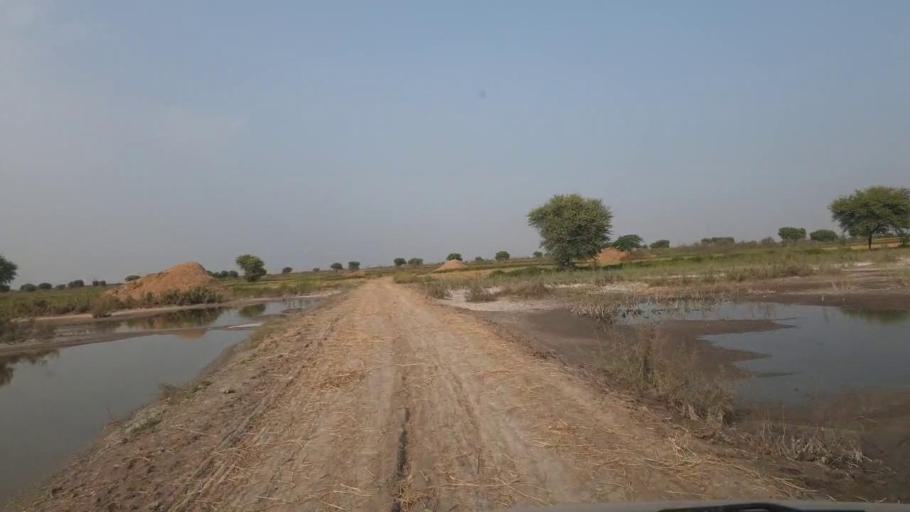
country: PK
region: Sindh
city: Matli
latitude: 25.0453
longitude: 68.7471
